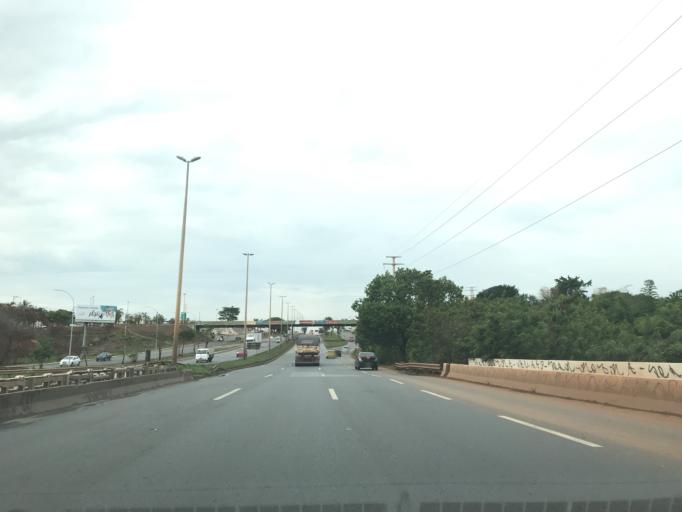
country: BR
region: Federal District
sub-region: Brasilia
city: Brasilia
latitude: -15.8453
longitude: -47.9541
